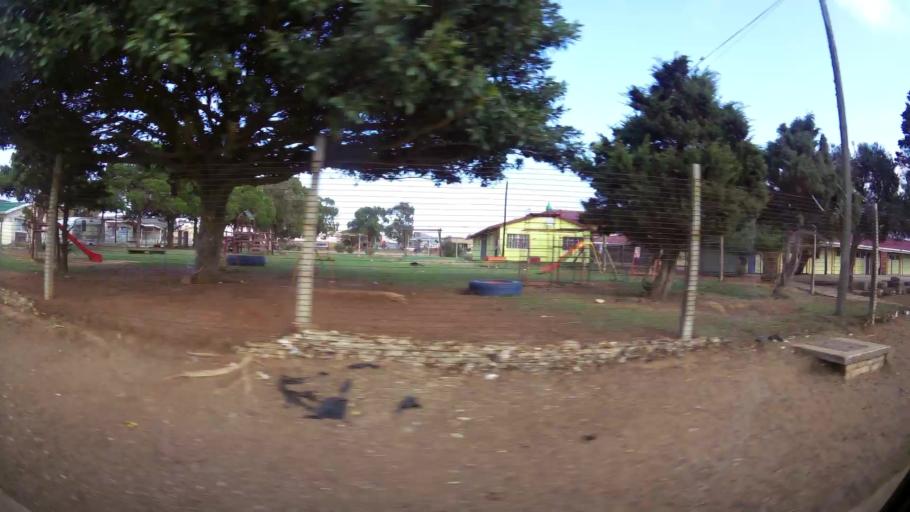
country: ZA
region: Eastern Cape
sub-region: Nelson Mandela Bay Metropolitan Municipality
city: Port Elizabeth
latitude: -33.9192
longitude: 25.5627
